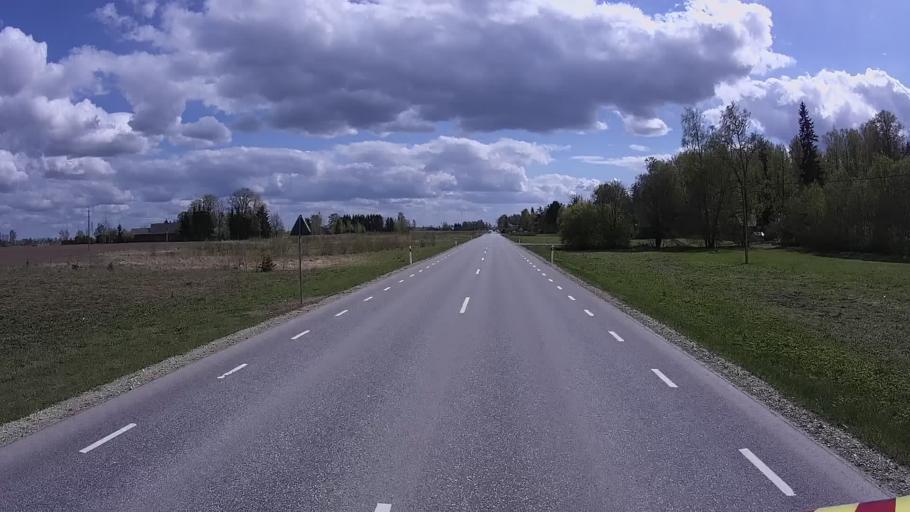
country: EE
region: Jogevamaa
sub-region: Jogeva linn
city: Jogeva
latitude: 58.7682
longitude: 26.3296
